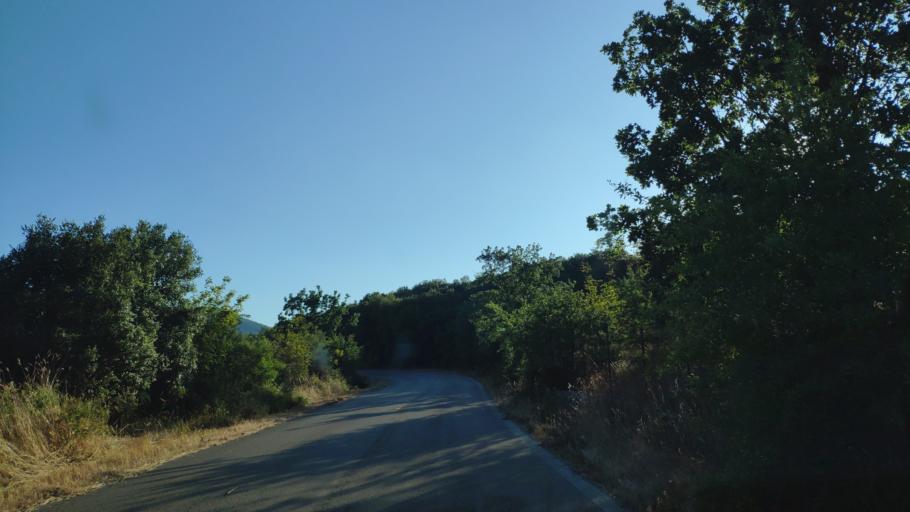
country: GR
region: West Greece
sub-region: Nomos Aitolias kai Akarnanias
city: Fitiai
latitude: 38.6352
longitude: 21.1671
